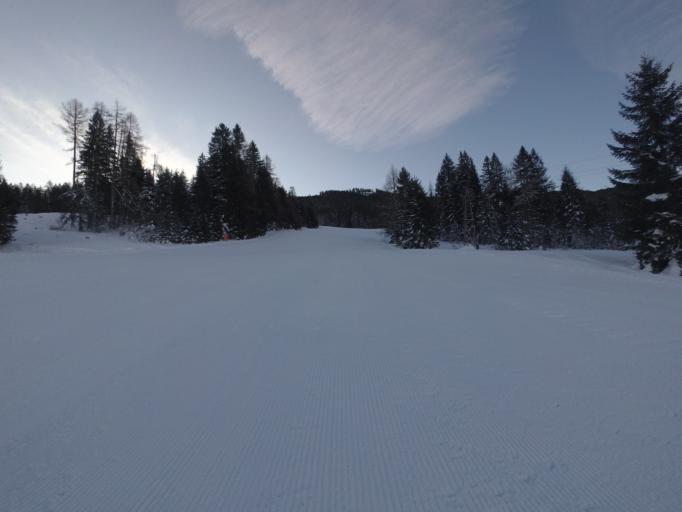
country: AT
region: Salzburg
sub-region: Politischer Bezirk Zell am See
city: Taxenbach
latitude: 47.2844
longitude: 13.0047
